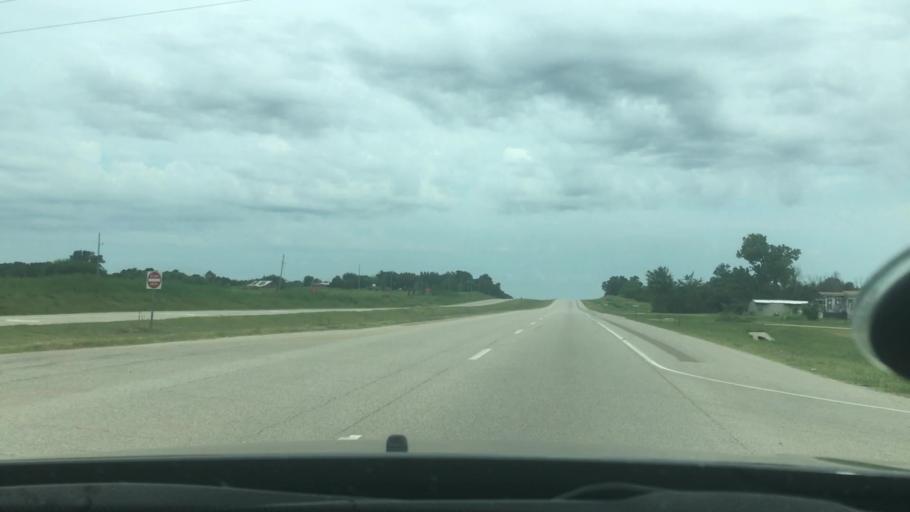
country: US
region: Oklahoma
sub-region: Pontotoc County
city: Byng
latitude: 34.9120
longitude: -96.6792
